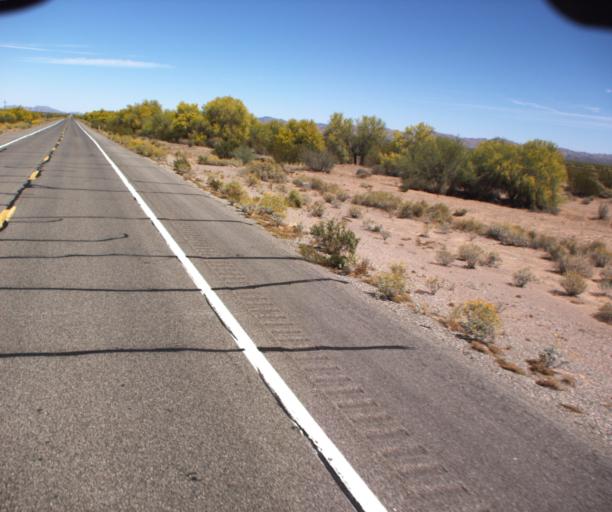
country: US
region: Arizona
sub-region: Pima County
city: Ajo
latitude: 32.5680
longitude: -112.8761
